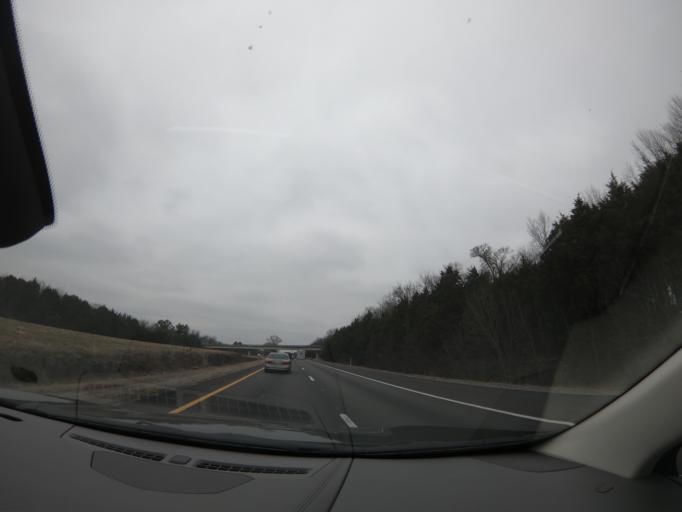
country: US
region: Tennessee
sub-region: Rutherford County
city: Plainview
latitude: 35.7445
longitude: -86.3380
